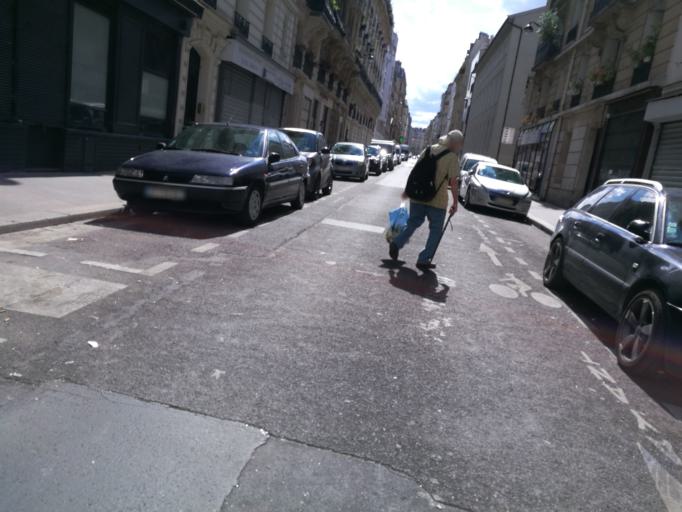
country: FR
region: Ile-de-France
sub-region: Paris
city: Saint-Ouen
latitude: 48.8946
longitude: 2.3406
